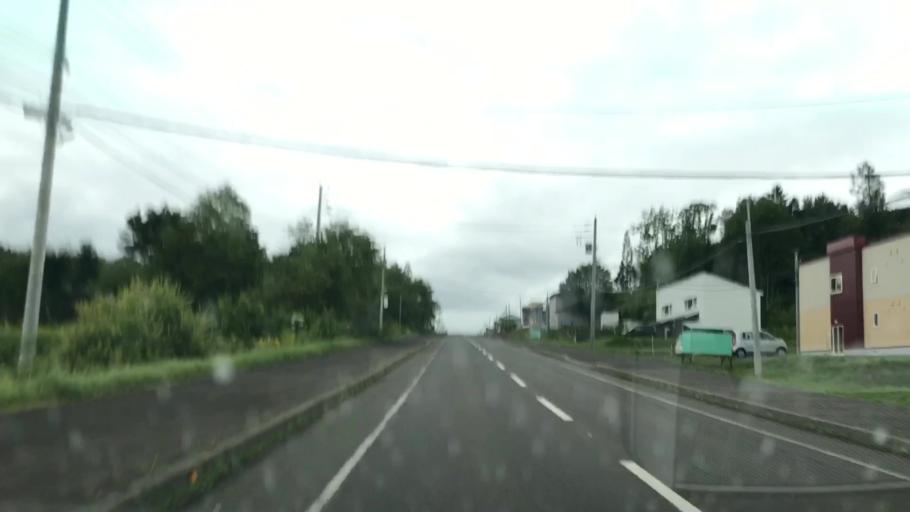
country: JP
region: Hokkaido
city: Niseko Town
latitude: 42.7984
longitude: 140.7045
